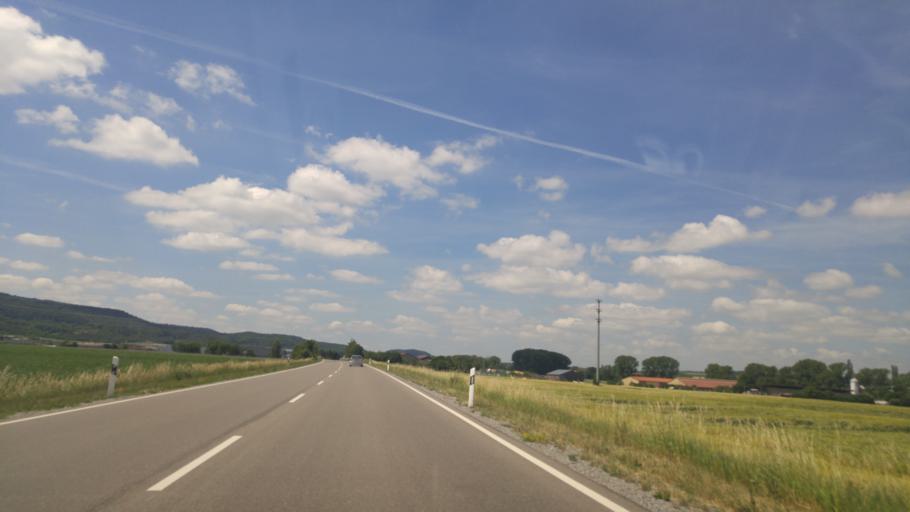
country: DE
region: Bavaria
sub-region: Regierungsbezirk Mittelfranken
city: Burgbernheim
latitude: 49.4627
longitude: 10.3227
